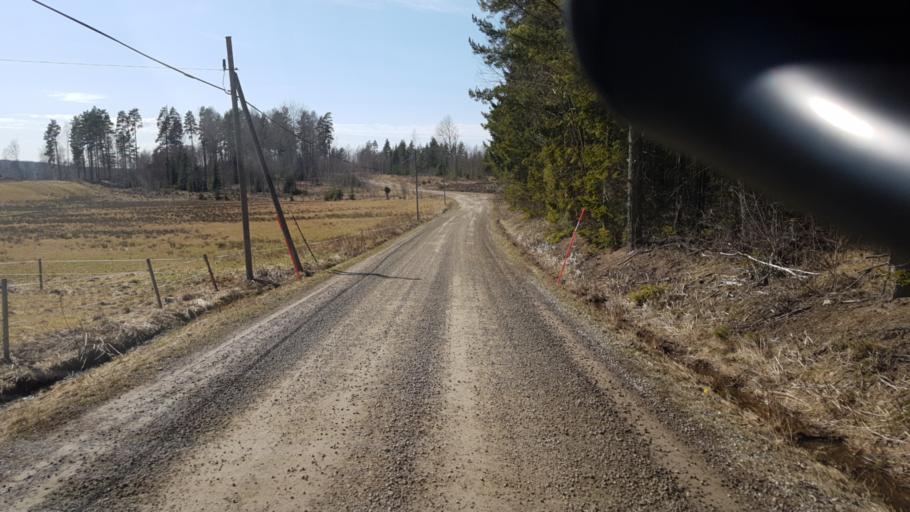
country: SE
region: Vaermland
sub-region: Arvika Kommun
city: Arvika
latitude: 59.5319
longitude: 12.8439
